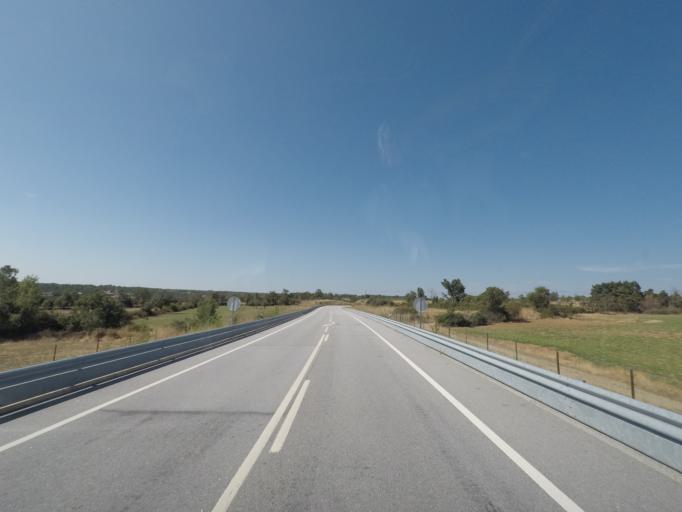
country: ES
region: Castille and Leon
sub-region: Provincia de Salamanca
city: Villarino de los Aires
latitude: 41.3651
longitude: -6.5254
